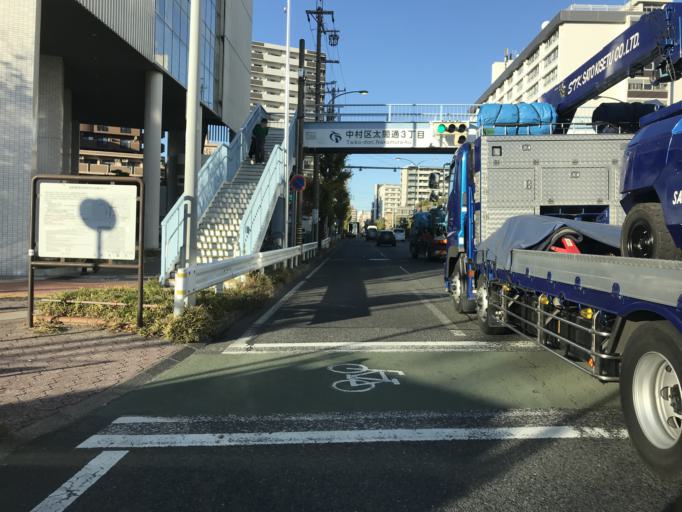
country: JP
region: Aichi
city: Nagoya-shi
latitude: 35.1679
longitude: 136.8723
